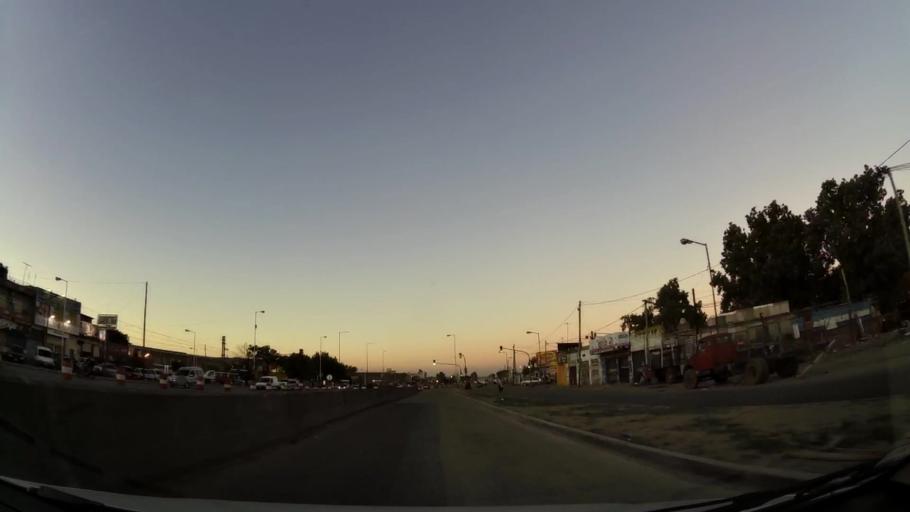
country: AR
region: Buenos Aires
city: San Justo
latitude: -34.7333
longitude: -58.6028
